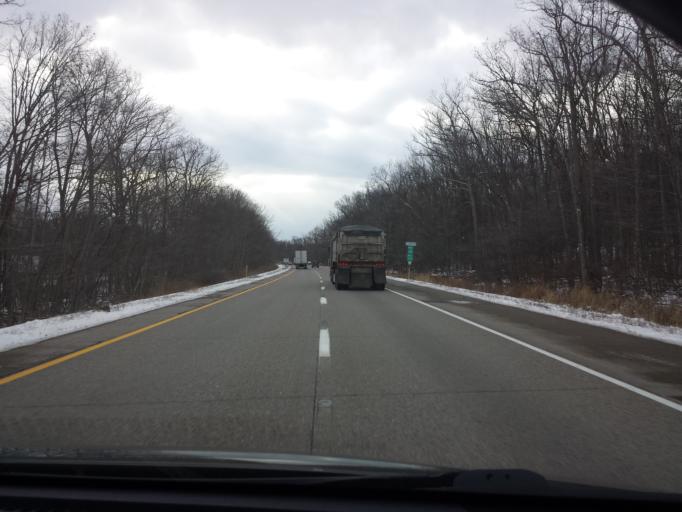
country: US
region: Pennsylvania
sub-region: Luzerne County
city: Conyngham
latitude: 41.0340
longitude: -76.0616
